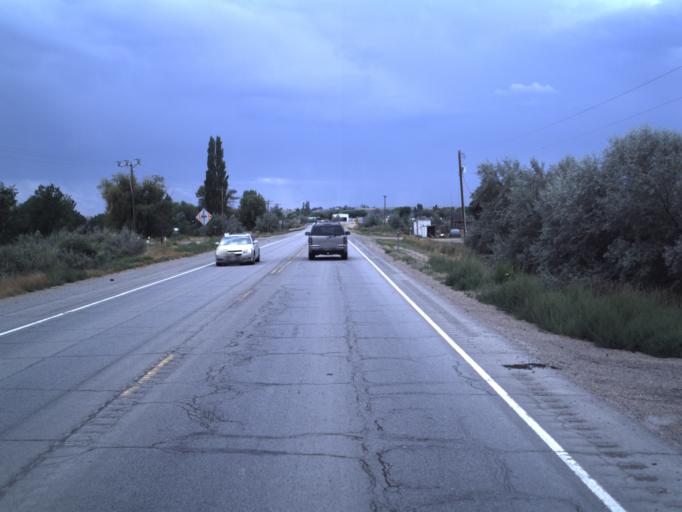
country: US
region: Utah
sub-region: Duchesne County
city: Roosevelt
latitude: 40.2048
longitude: -110.0676
